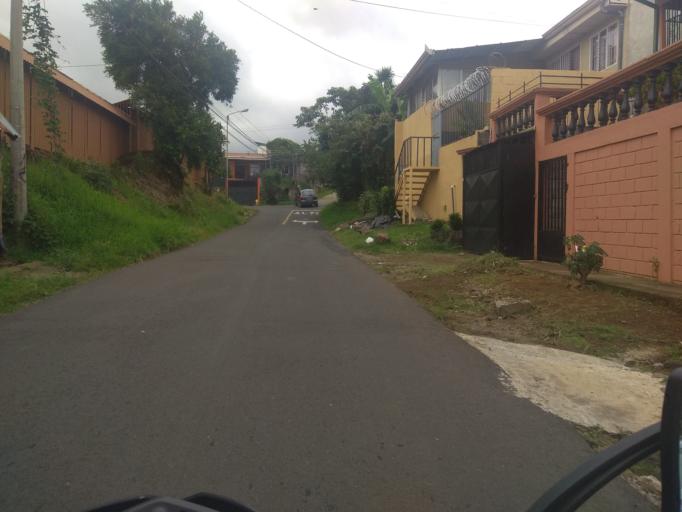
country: CR
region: Heredia
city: San Josecito
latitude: 10.0190
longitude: -84.1032
